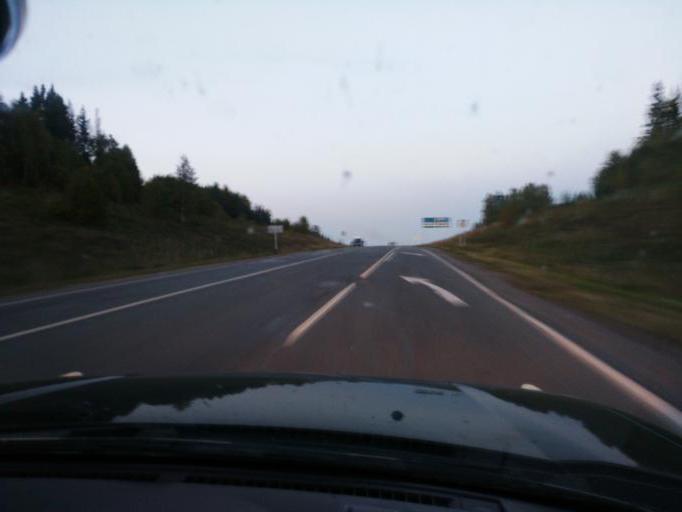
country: RU
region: Perm
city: Verkhnechusovskiye Gorodki
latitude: 58.2190
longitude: 57.1643
